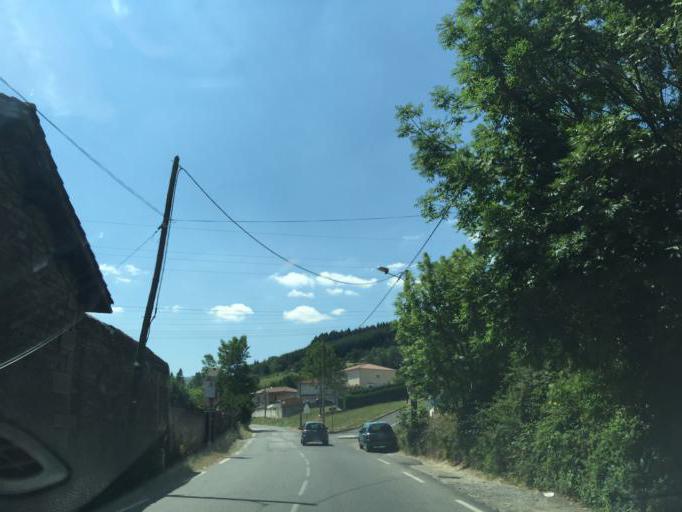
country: FR
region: Rhone-Alpes
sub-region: Departement de la Loire
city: Saint-Chamond
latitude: 45.4490
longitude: 4.5033
